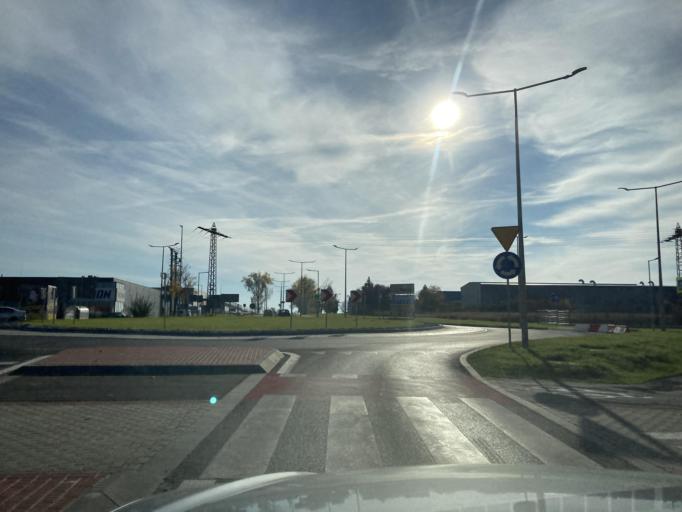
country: PL
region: Lubusz
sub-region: Powiat swiebodzinski
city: Swiebodzin
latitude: 52.2360
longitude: 15.5316
